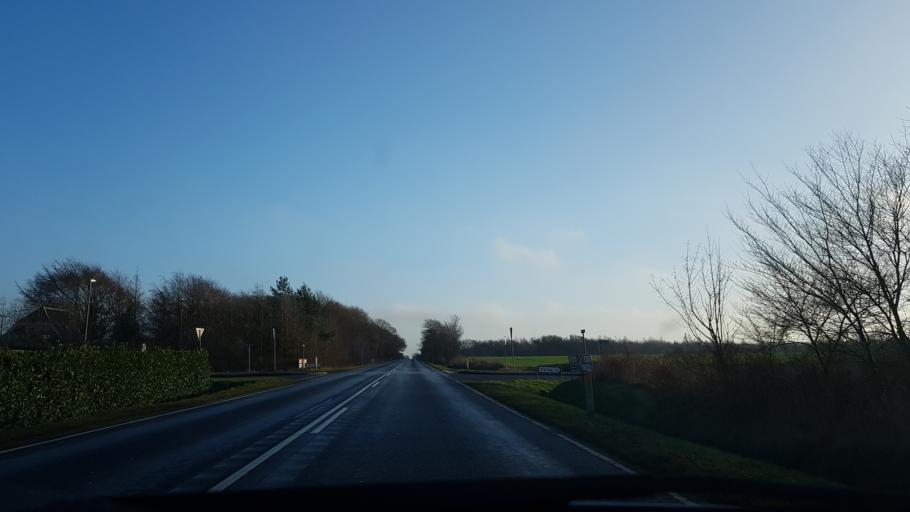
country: DK
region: South Denmark
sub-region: Haderslev Kommune
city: Vojens
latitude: 55.1968
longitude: 9.2002
